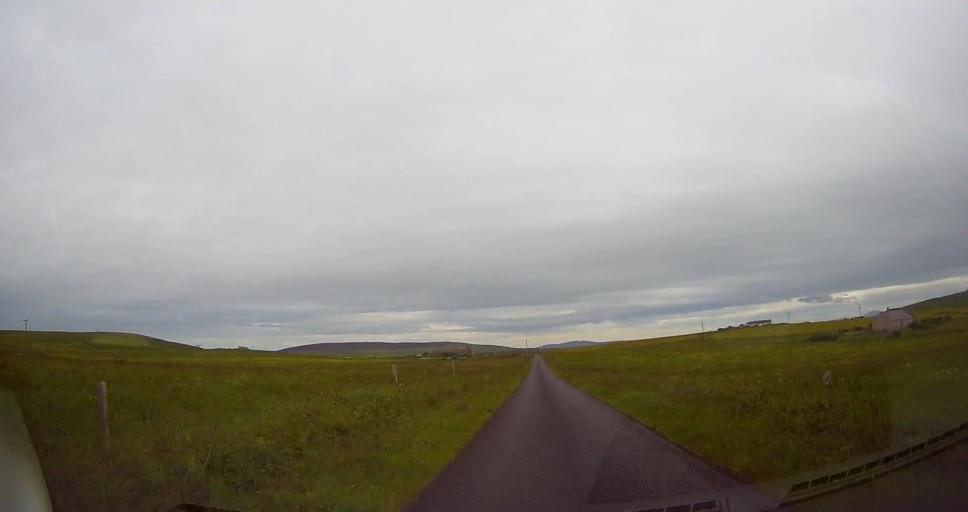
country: GB
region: Scotland
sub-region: Orkney Islands
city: Stromness
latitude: 59.1245
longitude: -3.2793
